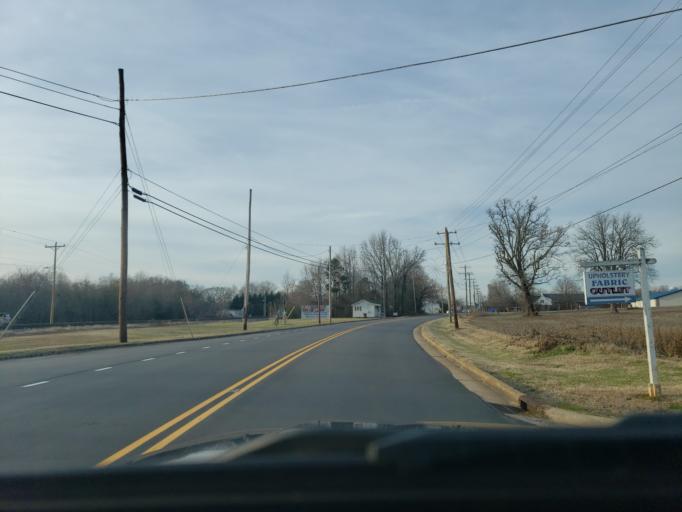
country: US
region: North Carolina
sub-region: Cleveland County
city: Boiling Springs
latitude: 35.3231
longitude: -81.7544
